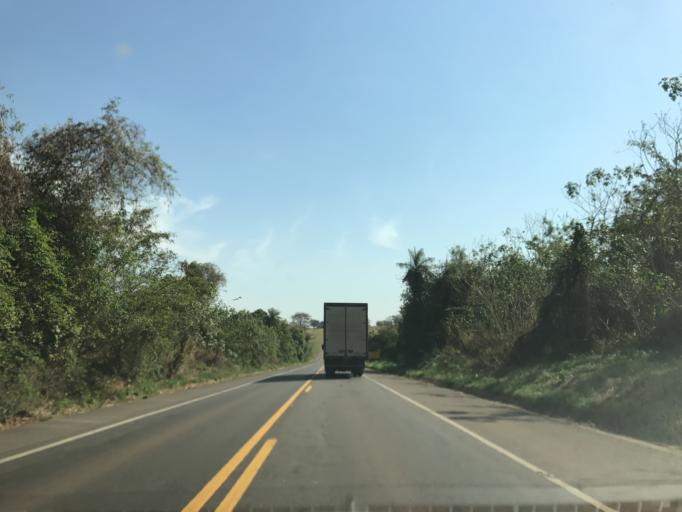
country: BR
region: Sao Paulo
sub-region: Jose Bonifacio
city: Jose Bonifacio
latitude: -21.1163
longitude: -49.8313
